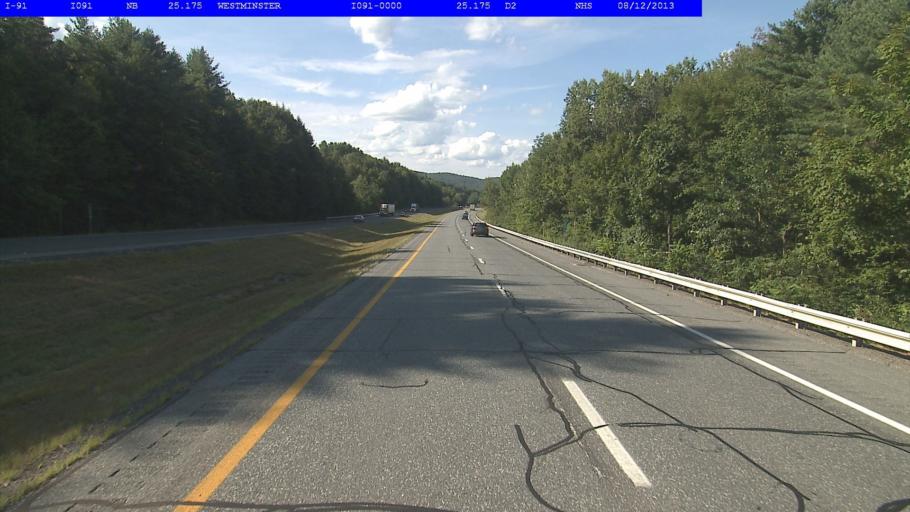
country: US
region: New Hampshire
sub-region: Cheshire County
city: Westmoreland
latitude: 43.0434
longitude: -72.4696
